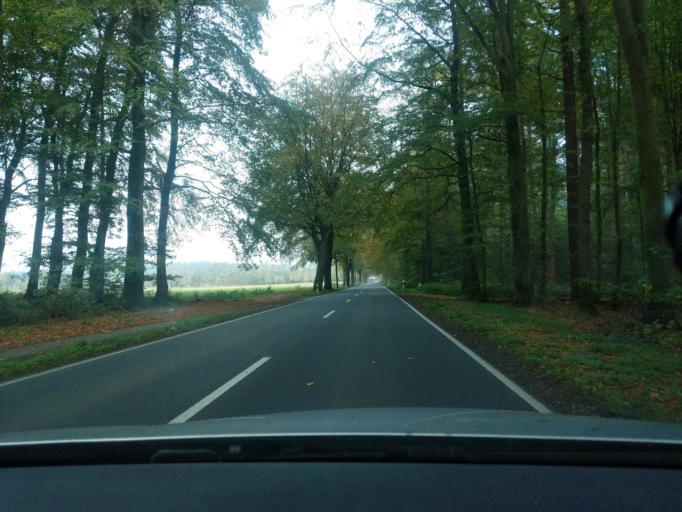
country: DE
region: Lower Saxony
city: Kranenburg
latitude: 53.6269
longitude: 9.1966
